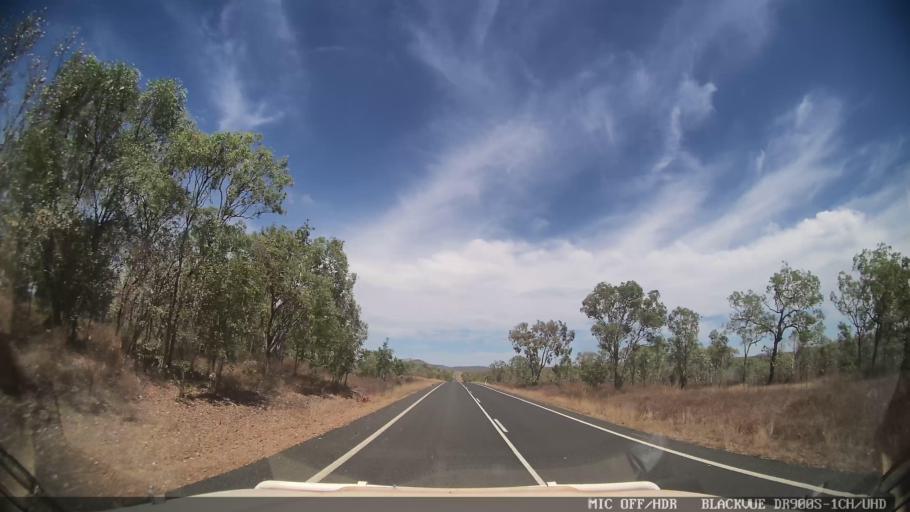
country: AU
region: Queensland
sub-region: Cook
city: Cooktown
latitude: -15.8835
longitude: 144.8590
